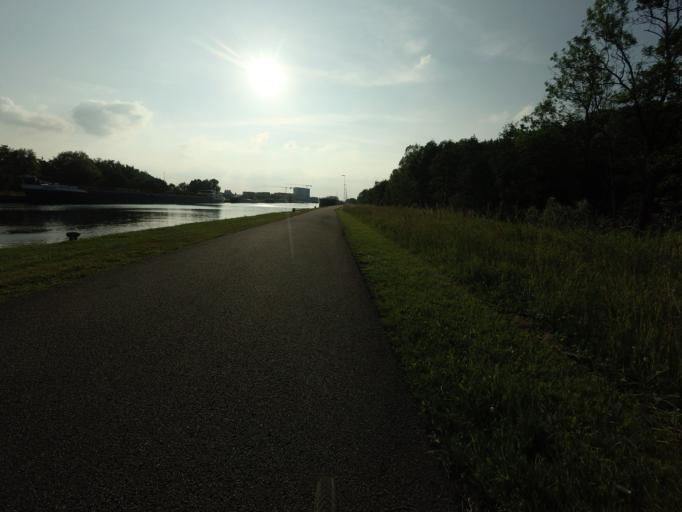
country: BE
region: Flanders
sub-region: Provincie Antwerpen
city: Ranst
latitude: 51.2217
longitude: 4.5555
